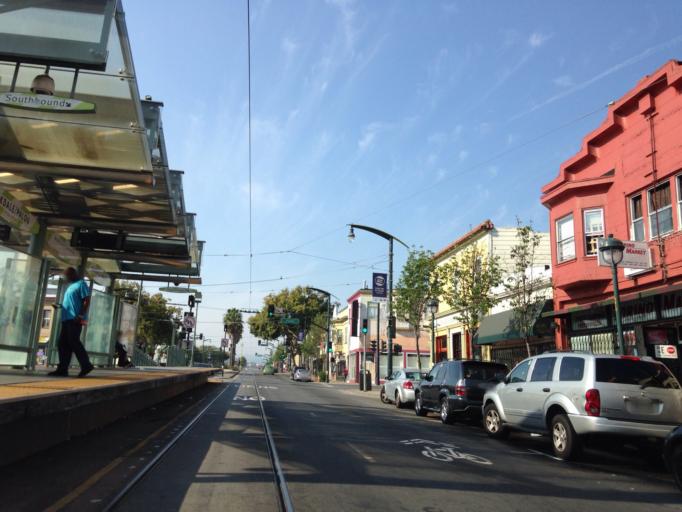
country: US
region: California
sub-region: San Francisco County
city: San Francisco
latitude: 37.7345
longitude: -122.3909
